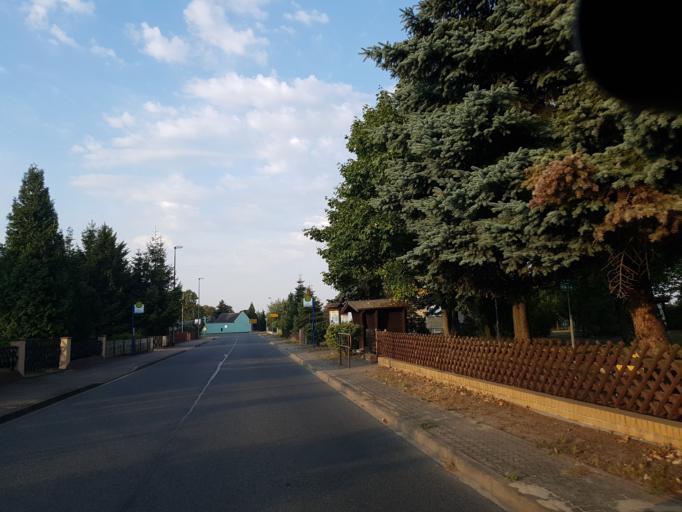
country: DE
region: Brandenburg
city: Hohenleipisch
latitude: 51.4711
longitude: 13.5677
